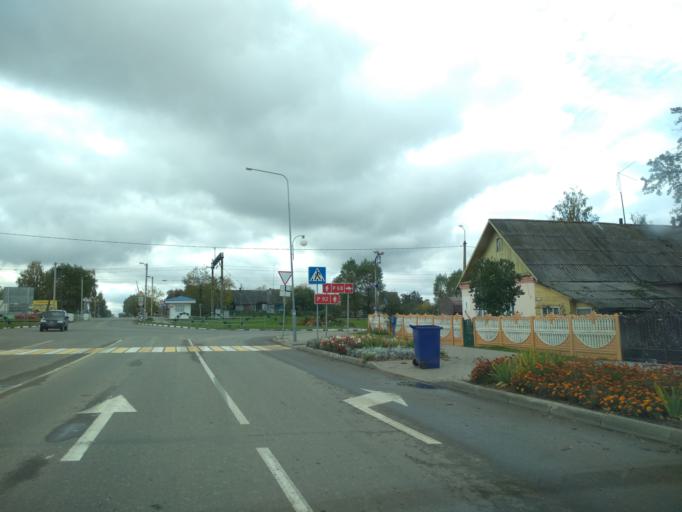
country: BY
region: Minsk
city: Mar''ina Horka
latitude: 53.5176
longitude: 28.1403
